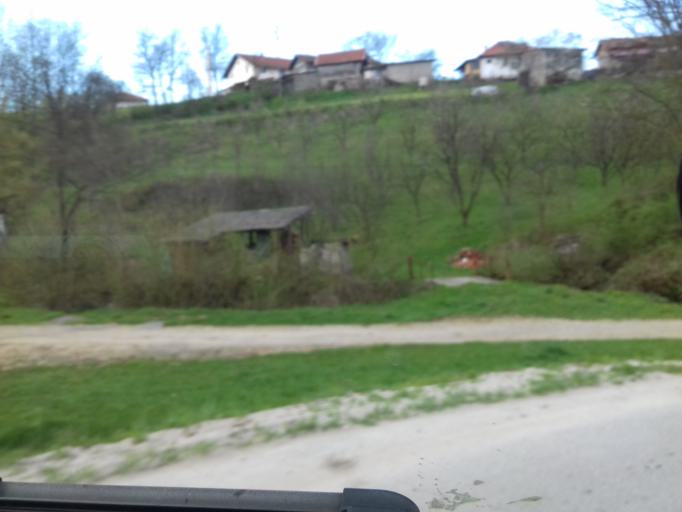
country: BA
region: Federation of Bosnia and Herzegovina
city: Tesanjka
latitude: 44.6445
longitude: 18.0256
